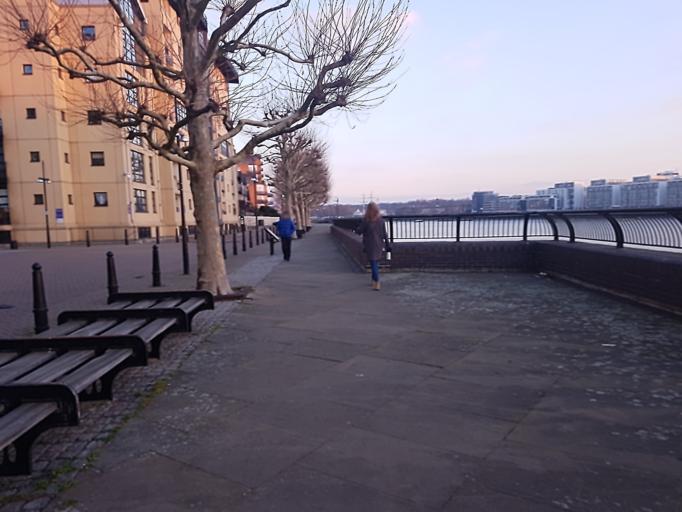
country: GB
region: England
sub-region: Greater London
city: Poplar
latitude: 51.4872
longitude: -0.0206
